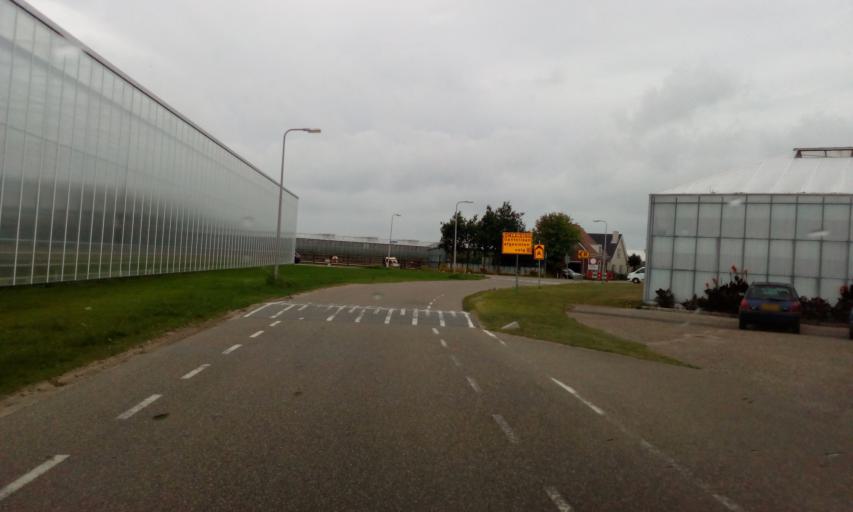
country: NL
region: South Holland
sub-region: Gemeente Westland
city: Monster
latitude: 52.0132
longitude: 4.1821
